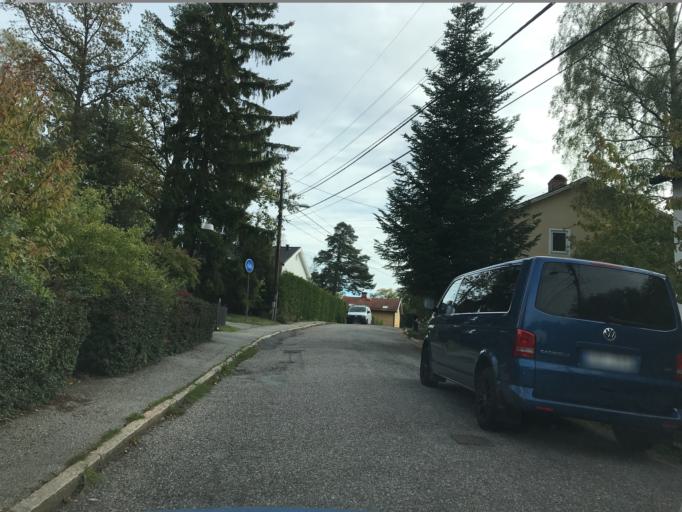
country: SE
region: Stockholm
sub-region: Huddinge Kommun
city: Huddinge
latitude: 59.2756
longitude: 17.9751
